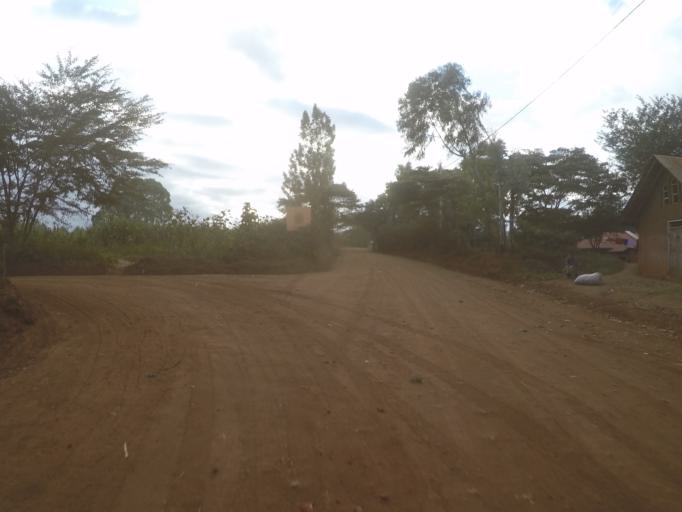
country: TZ
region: Arusha
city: Kiratu
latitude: -3.3227
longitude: 35.6644
